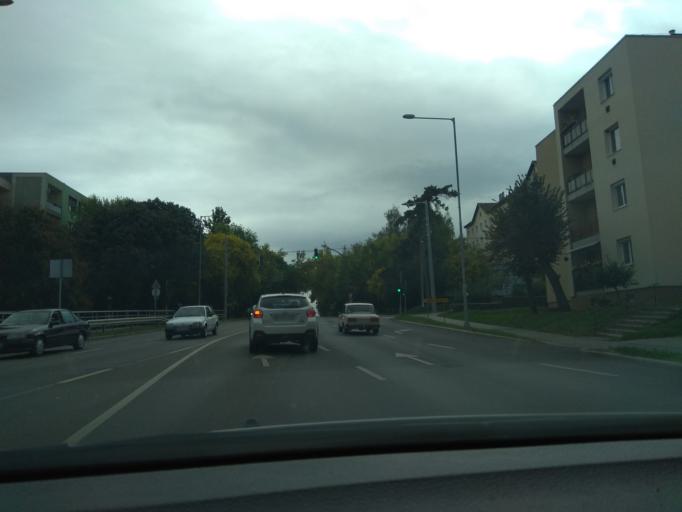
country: HU
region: Heves
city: Eger
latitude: 47.8853
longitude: 20.3809
